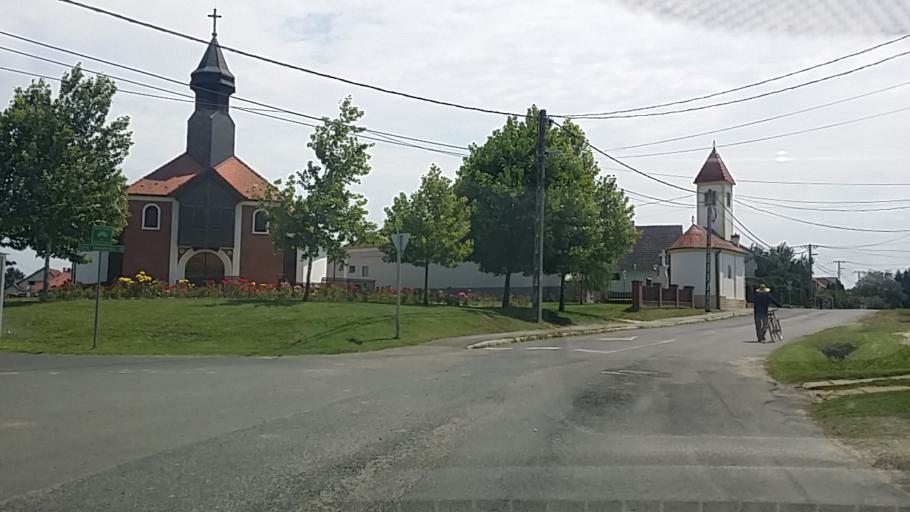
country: HR
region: Medimurska
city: Kotoriba
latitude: 46.3851
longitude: 16.8307
